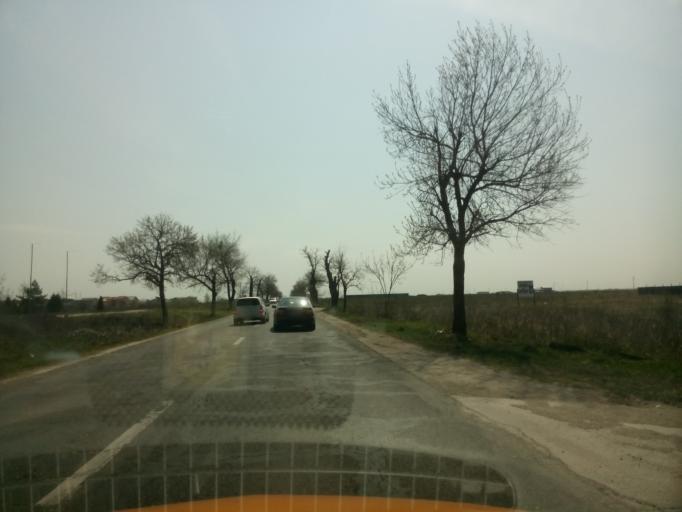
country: RO
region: Ilfov
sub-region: Comuna Glina
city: Glina
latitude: 44.3411
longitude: 26.2334
